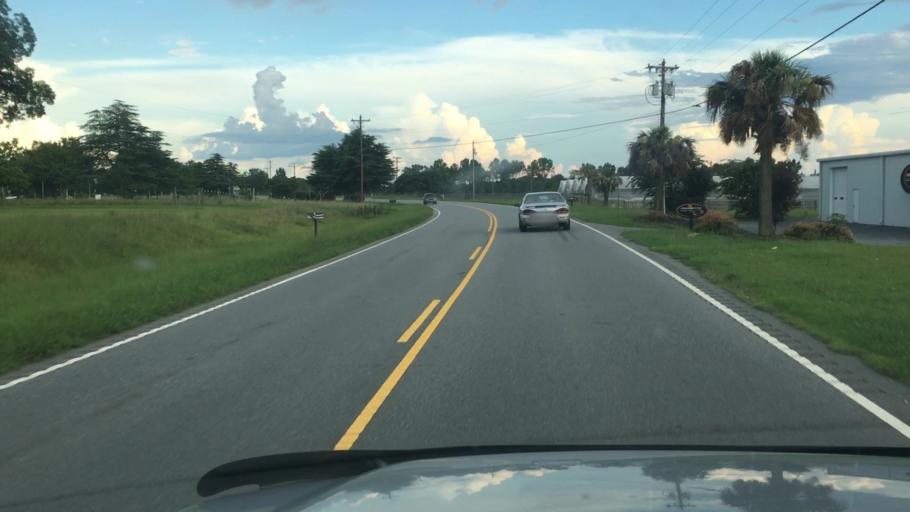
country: US
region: South Carolina
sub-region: Cherokee County
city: Gaffney
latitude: 35.1074
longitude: -81.6977
